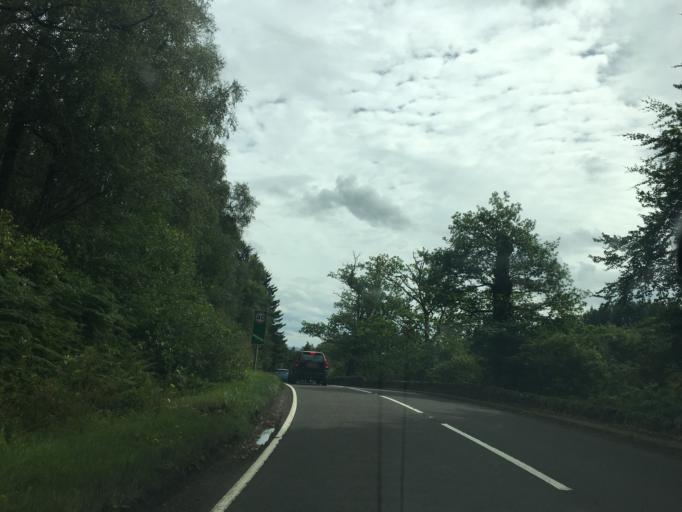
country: GB
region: Scotland
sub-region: Stirling
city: Callander
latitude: 56.2494
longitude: -4.2571
